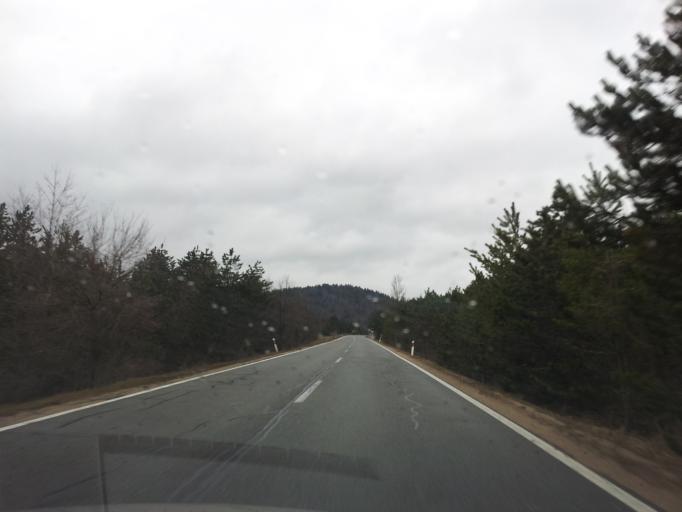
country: HR
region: Licko-Senjska
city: Jezerce
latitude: 44.7812
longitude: 15.6888
